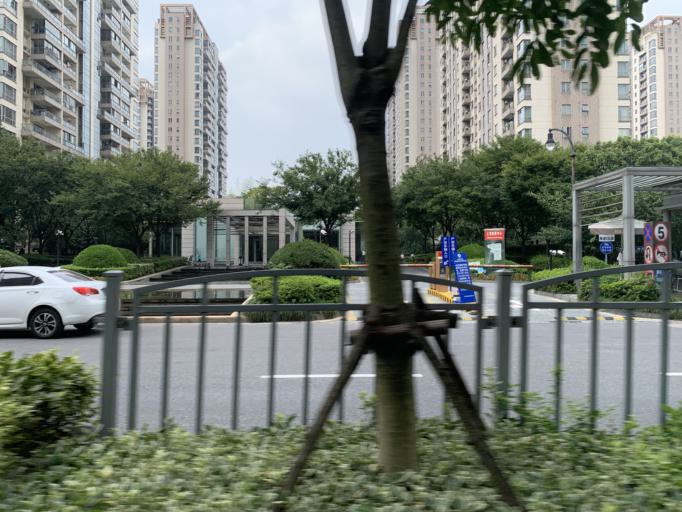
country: CN
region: Shanghai Shi
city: Huamu
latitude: 31.2292
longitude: 121.5616
